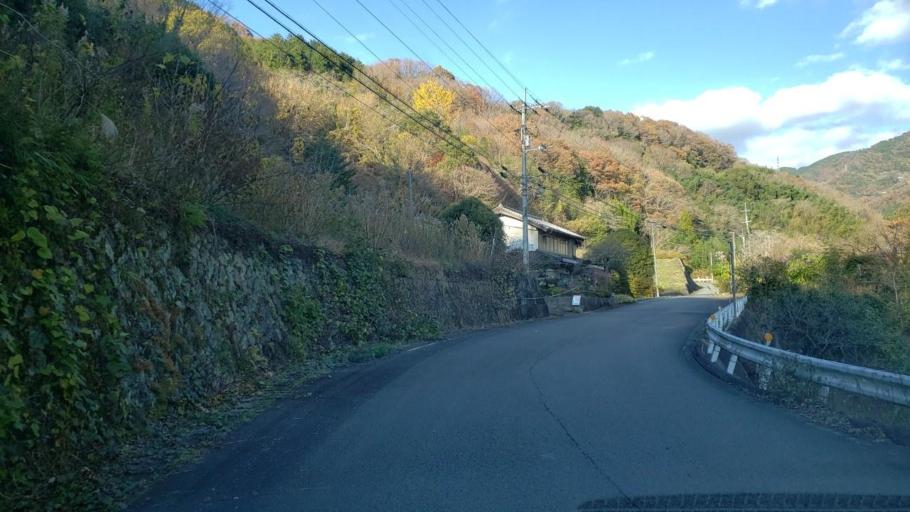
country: JP
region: Tokushima
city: Wakimachi
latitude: 34.0967
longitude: 134.0681
